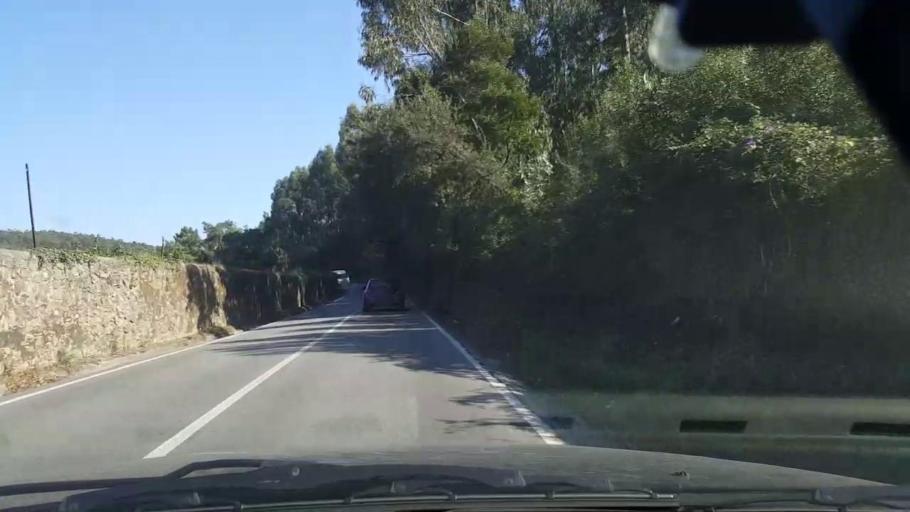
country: PT
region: Porto
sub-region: Maia
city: Gemunde
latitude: 41.3256
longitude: -8.6494
